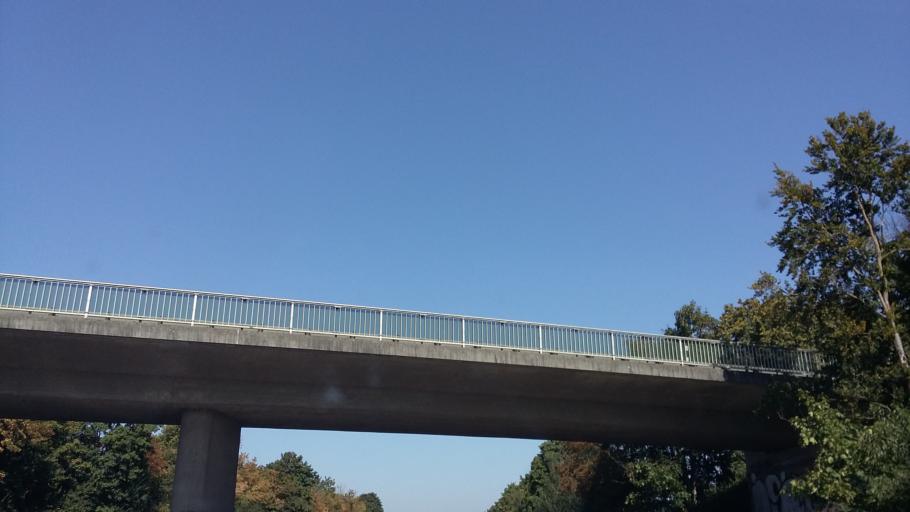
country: DE
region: Bavaria
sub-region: Swabia
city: Oberottmarshausen
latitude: 48.2371
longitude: 10.8692
